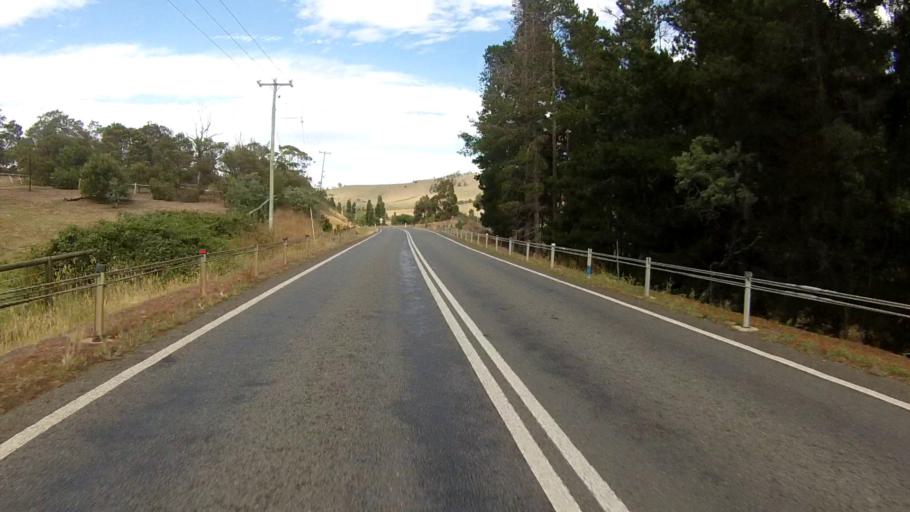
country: AU
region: Tasmania
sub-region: Brighton
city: Old Beach
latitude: -42.6709
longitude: 147.3647
